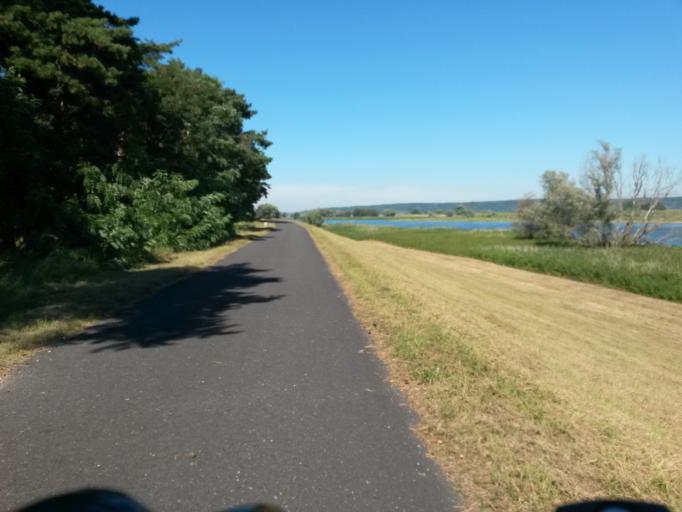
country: PL
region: West Pomeranian Voivodeship
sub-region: Powiat gryfinski
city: Cedynia
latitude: 52.8884
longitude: 14.1580
